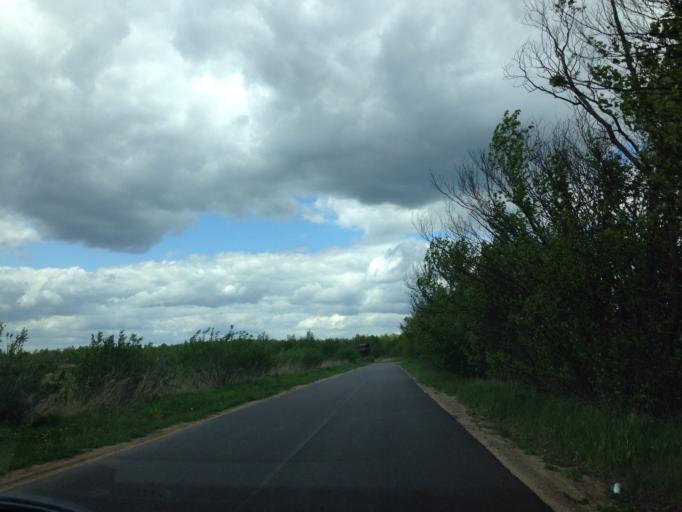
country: PL
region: Podlasie
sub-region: Powiat bialostocki
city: Tykocin
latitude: 53.2966
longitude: 22.6060
